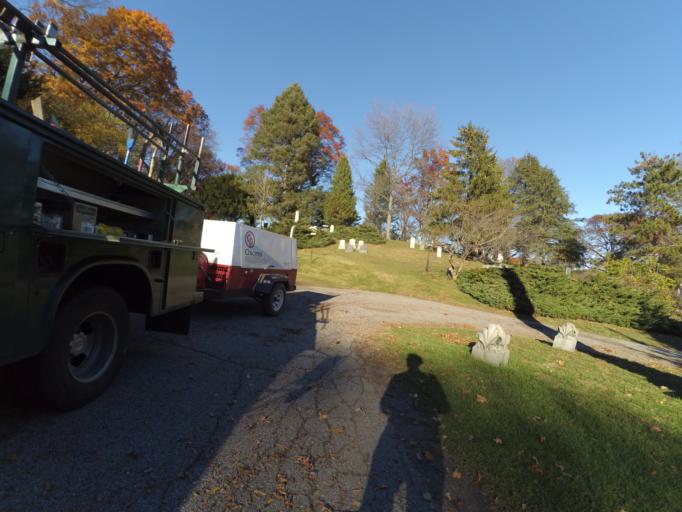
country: US
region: Massachusetts
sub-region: Middlesex County
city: Cambridge
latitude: 42.3694
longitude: -71.1434
